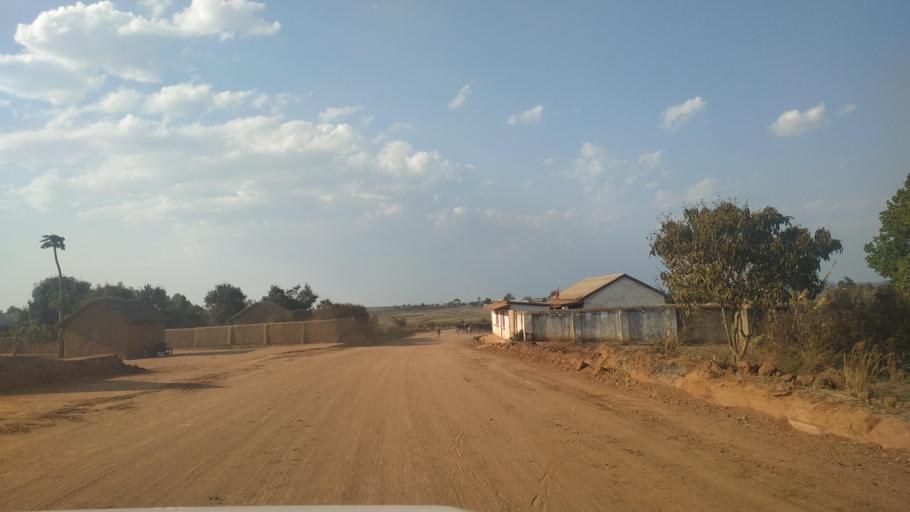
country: MG
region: Alaotra Mangoro
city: Ambatondrazaka
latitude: -17.8920
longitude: 48.2540
